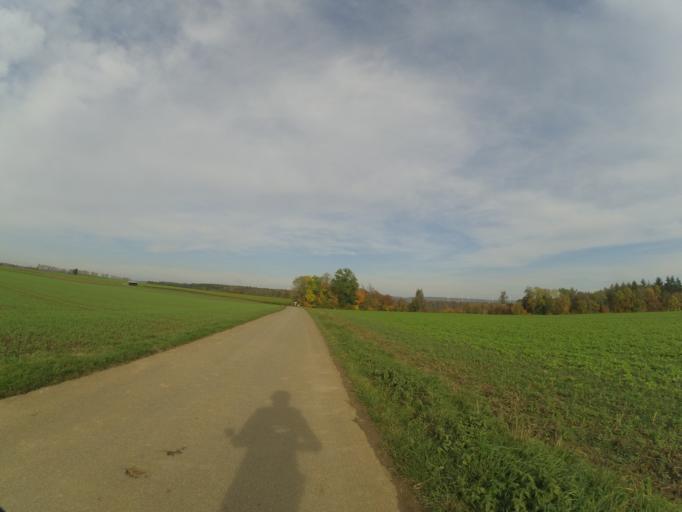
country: DE
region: Baden-Wuerttemberg
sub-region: Tuebingen Region
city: Blaubeuren
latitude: 48.4384
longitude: 9.8634
